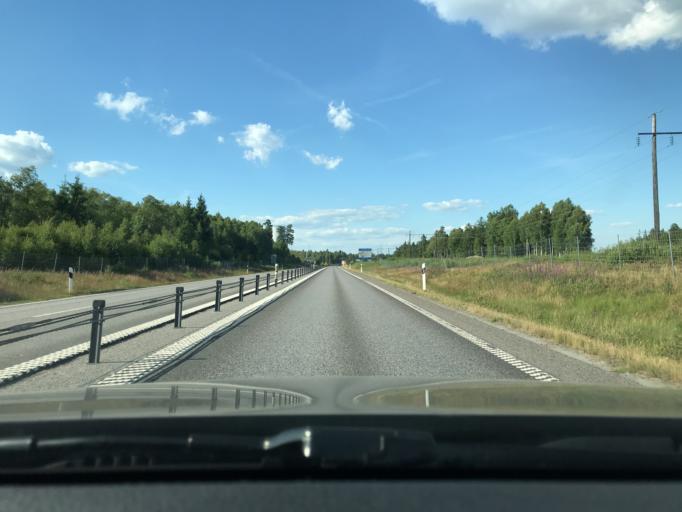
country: SE
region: Kronoberg
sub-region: Almhults Kommun
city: AElmhult
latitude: 56.5269
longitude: 14.1416
